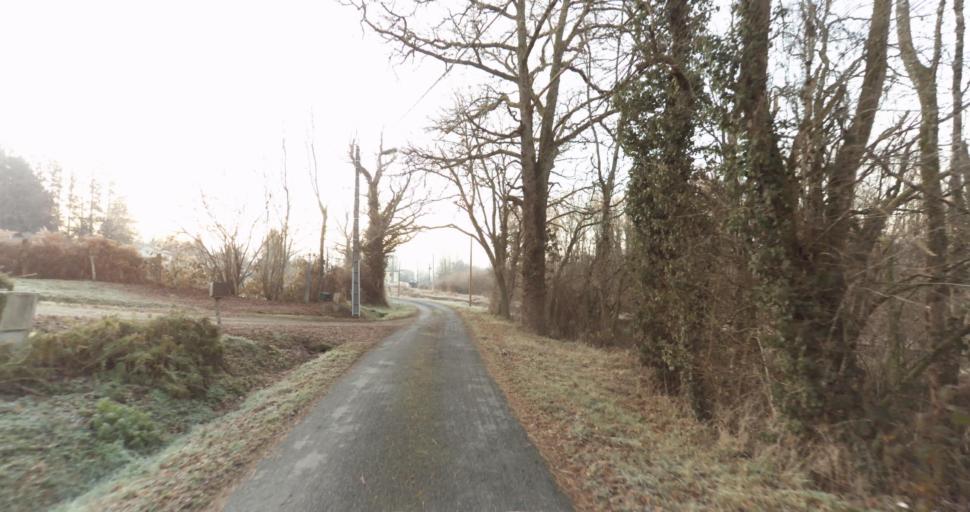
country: FR
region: Limousin
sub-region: Departement de la Haute-Vienne
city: Aixe-sur-Vienne
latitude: 45.8068
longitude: 1.1222
